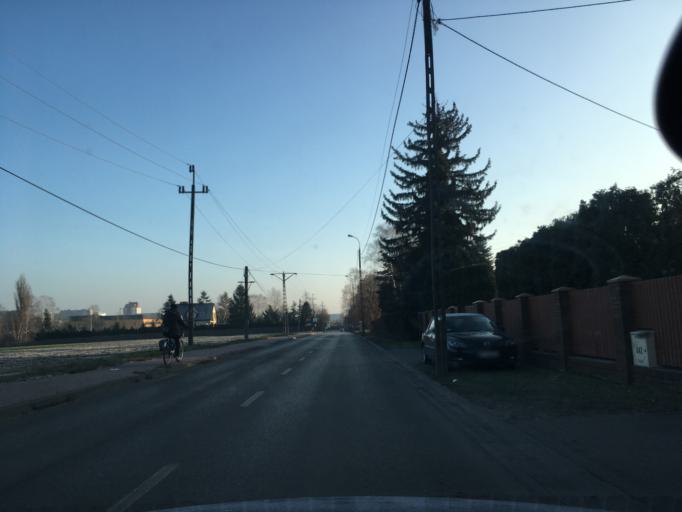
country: PL
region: Masovian Voivodeship
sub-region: Powiat piaseczynski
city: Piaseczno
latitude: 52.0710
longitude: 21.0067
